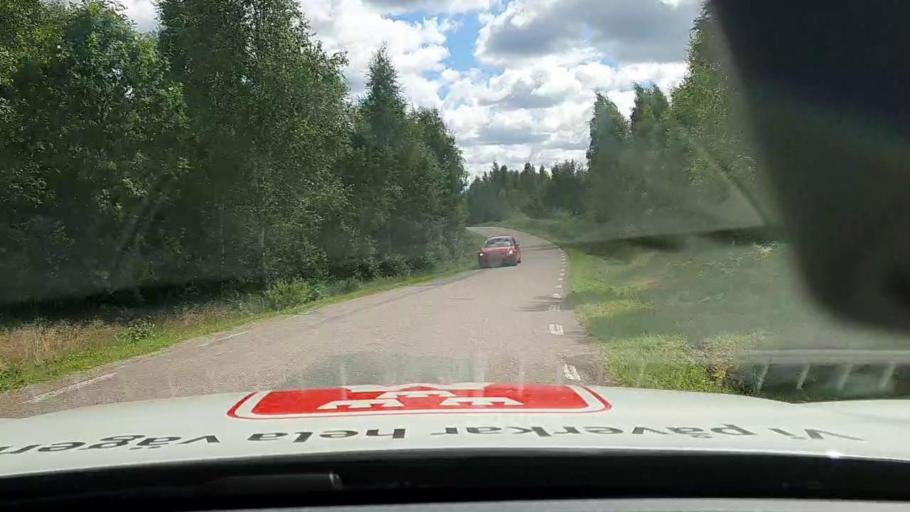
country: SE
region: Vaestra Goetaland
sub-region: Karlsborgs Kommun
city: Molltorp
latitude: 58.6068
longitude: 14.3016
